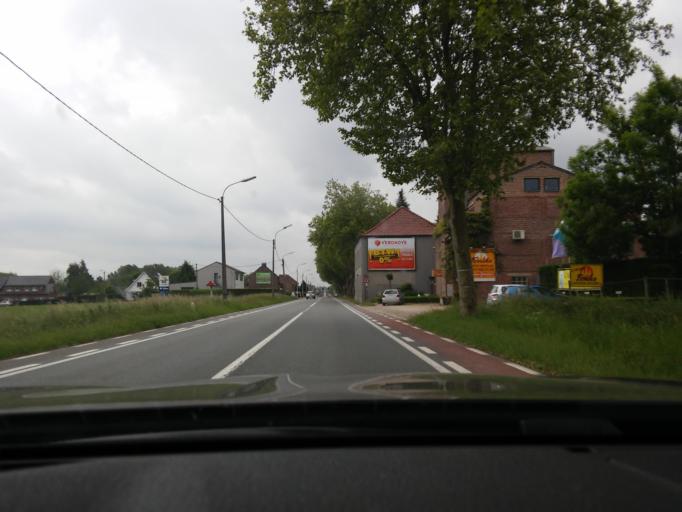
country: BE
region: Flanders
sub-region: Provincie Vlaams-Brabant
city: Ternat
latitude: 50.8589
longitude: 4.1557
